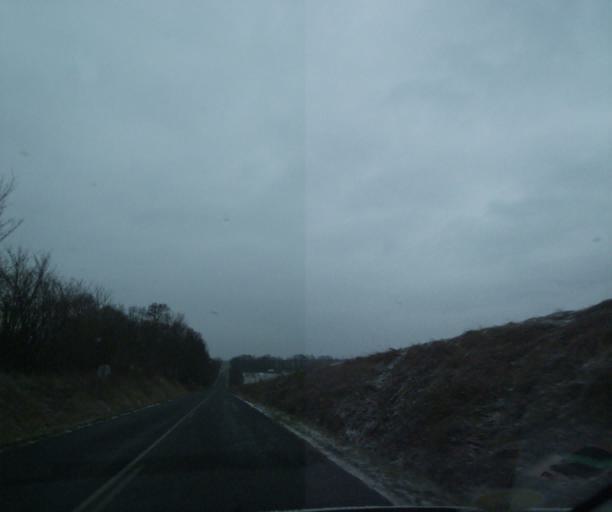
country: FR
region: Champagne-Ardenne
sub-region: Departement de la Haute-Marne
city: Wassy
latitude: 48.4281
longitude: 4.9690
